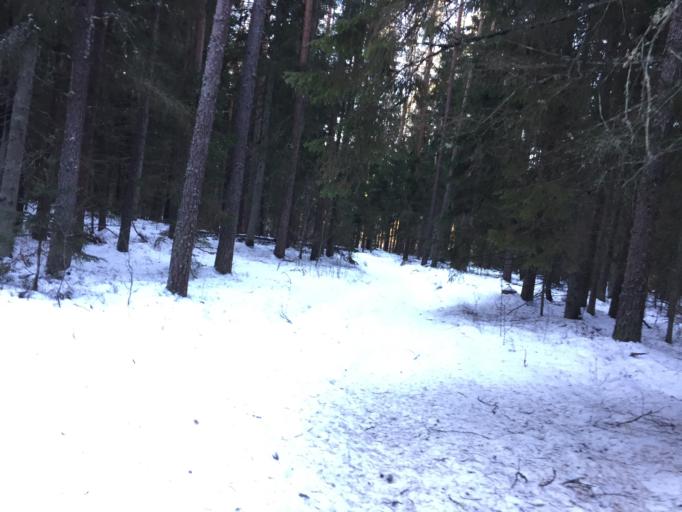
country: LV
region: Kegums
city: Kegums
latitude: 56.7305
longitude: 24.6409
